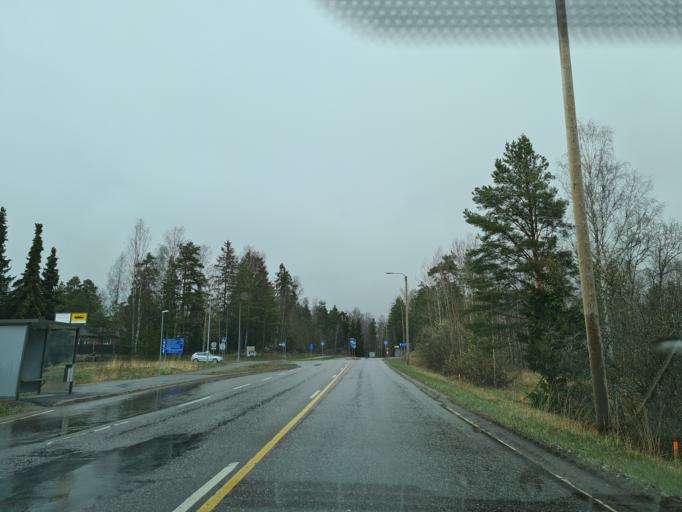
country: FI
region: Uusimaa
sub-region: Helsinki
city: Kirkkonummi
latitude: 60.0937
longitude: 24.4116
